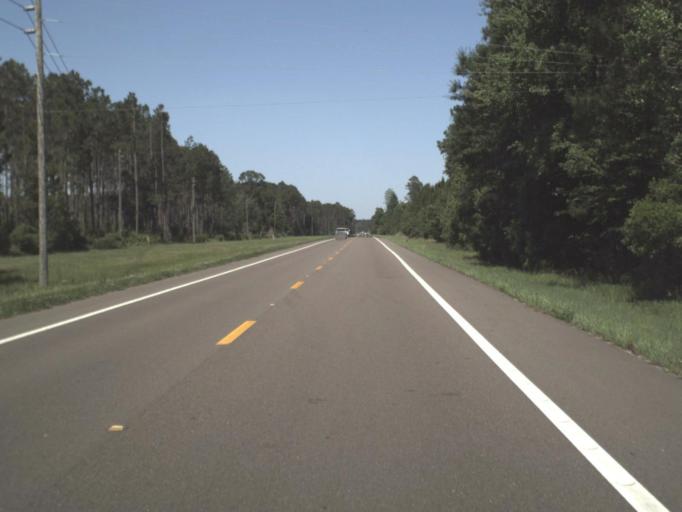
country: US
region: Florida
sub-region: Duval County
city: Baldwin
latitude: 30.2966
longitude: -82.0402
